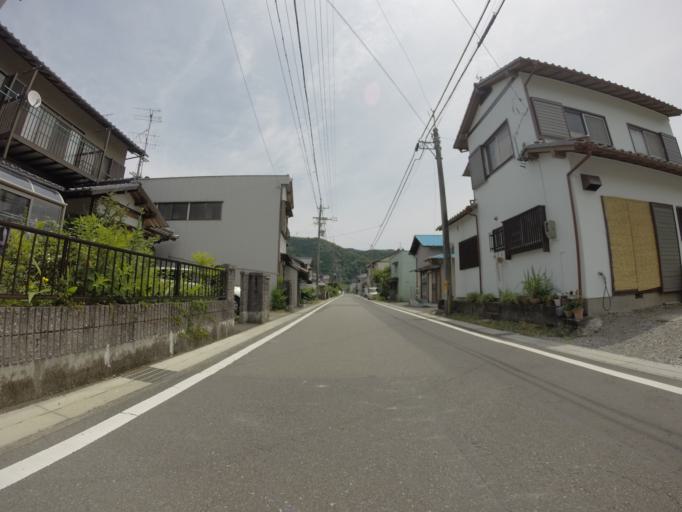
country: JP
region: Shizuoka
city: Shizuoka-shi
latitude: 35.0068
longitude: 138.2800
